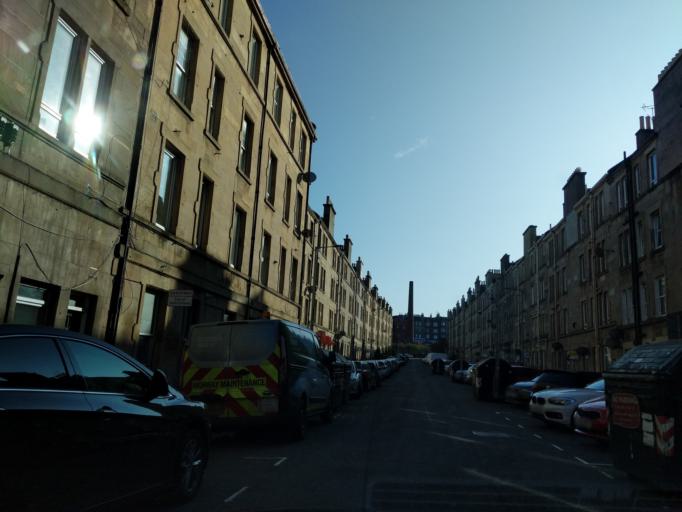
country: GB
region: Scotland
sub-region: Edinburgh
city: Colinton
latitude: 55.9372
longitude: -3.2340
